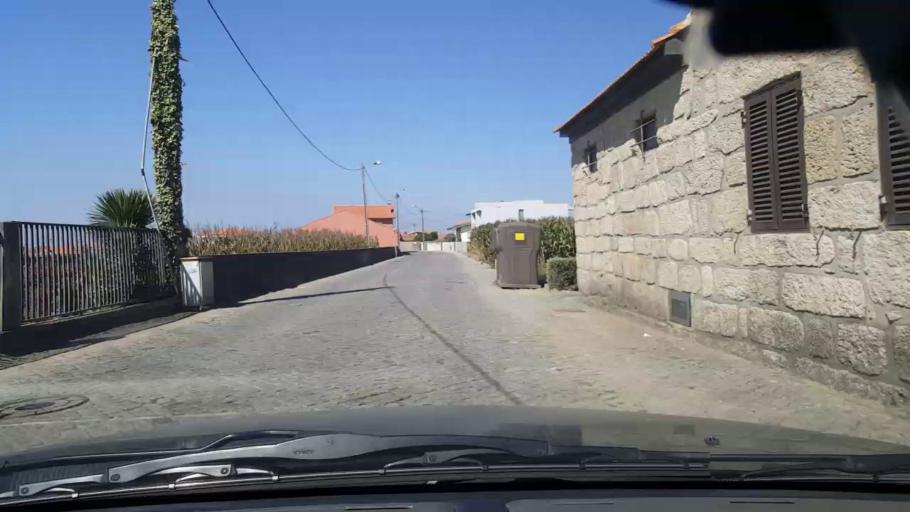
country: PT
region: Porto
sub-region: Matosinhos
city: Lavra
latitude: 41.2805
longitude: -8.7229
